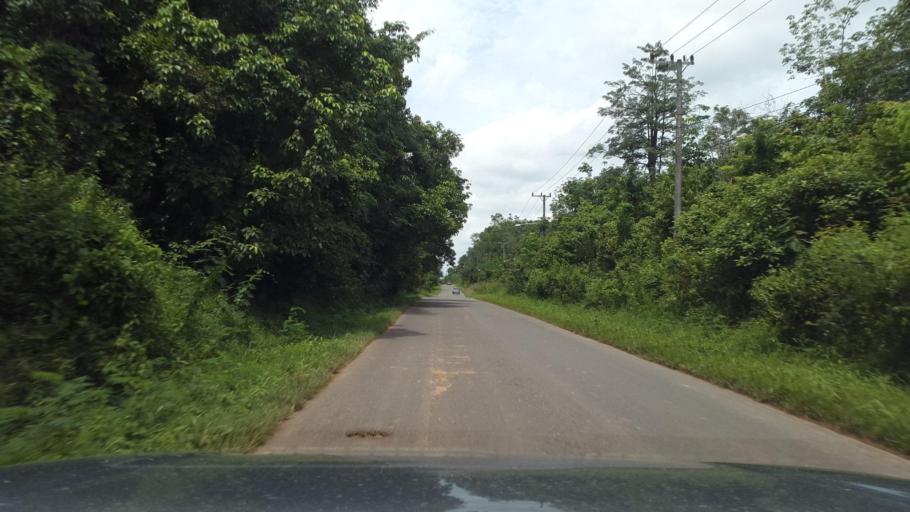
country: ID
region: South Sumatra
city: Gunungmegang Dalam
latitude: -3.3532
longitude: 103.9244
